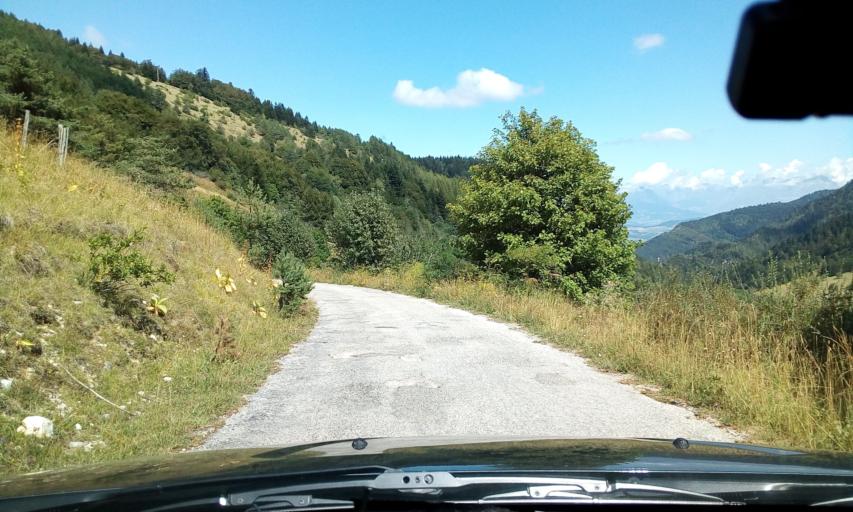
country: FR
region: Rhone-Alpes
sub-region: Departement de l'Isere
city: Mens
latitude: 44.7229
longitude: 5.6730
